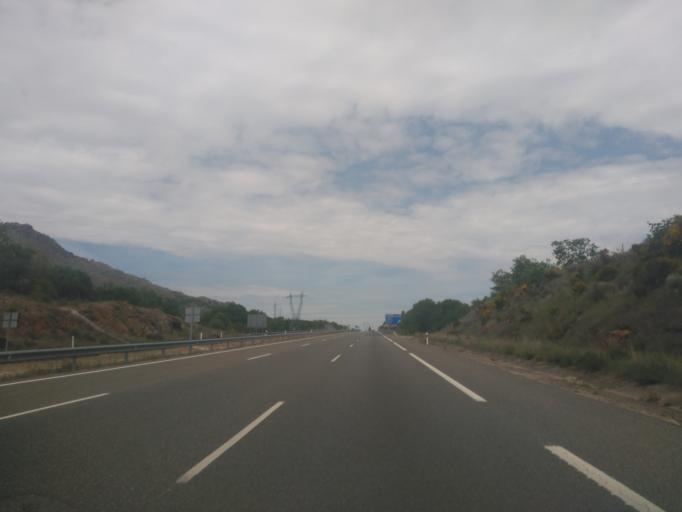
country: ES
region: Castille and Leon
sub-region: Provincia de Salamanca
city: Vallejera de Riofrio
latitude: 40.4037
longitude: -5.7308
